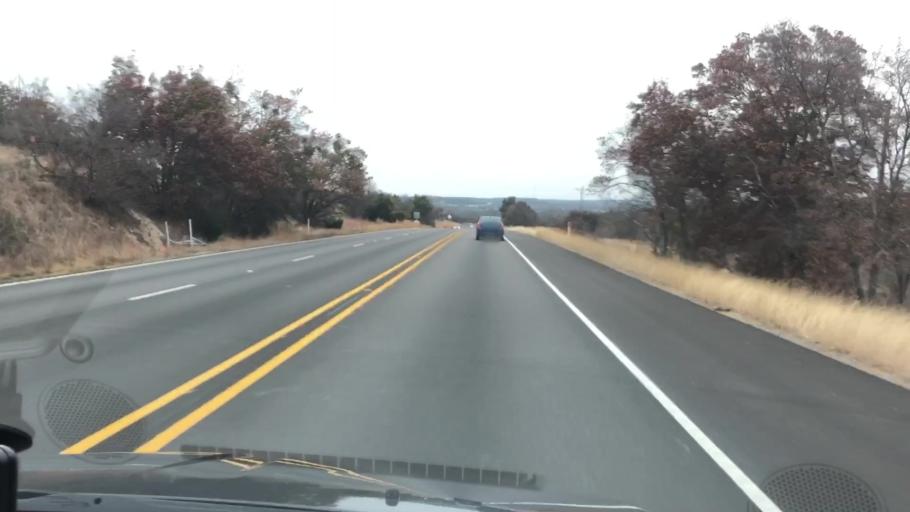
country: US
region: Texas
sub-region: Erath County
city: Stephenville
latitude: 32.3578
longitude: -98.1742
